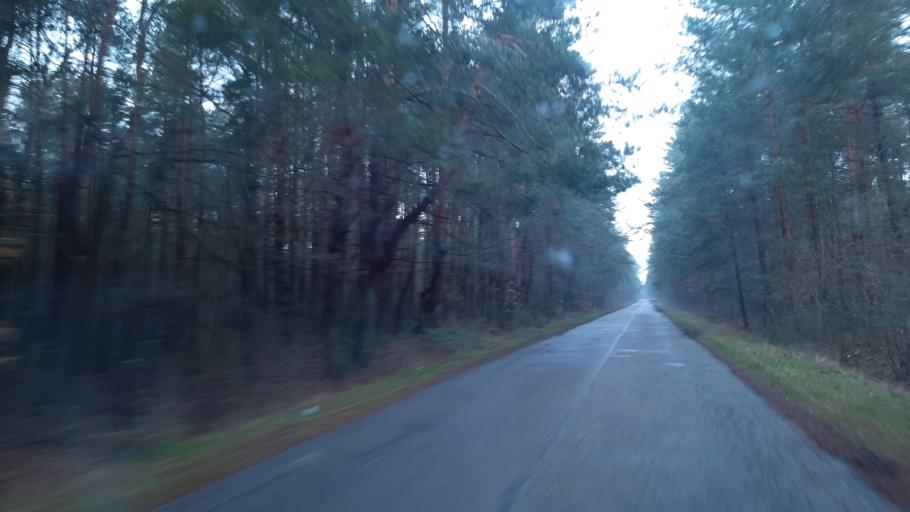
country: PL
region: Lublin Voivodeship
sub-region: Powiat lubartowski
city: Kamionka
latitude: 51.4844
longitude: 22.4755
